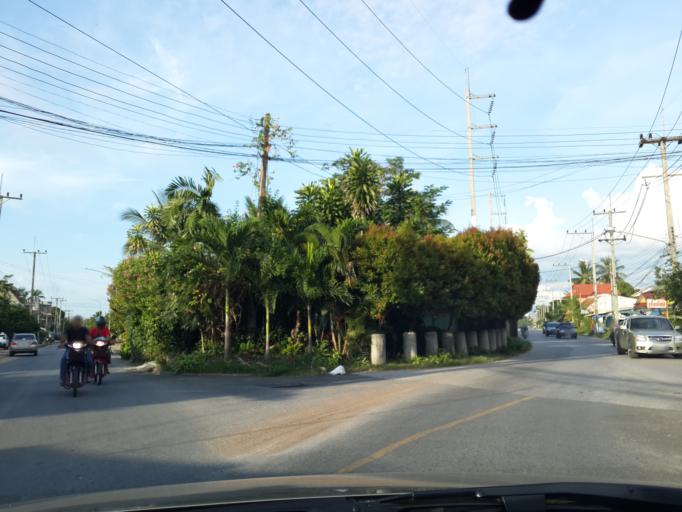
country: TH
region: Yala
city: Yala
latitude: 6.5327
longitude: 101.2624
